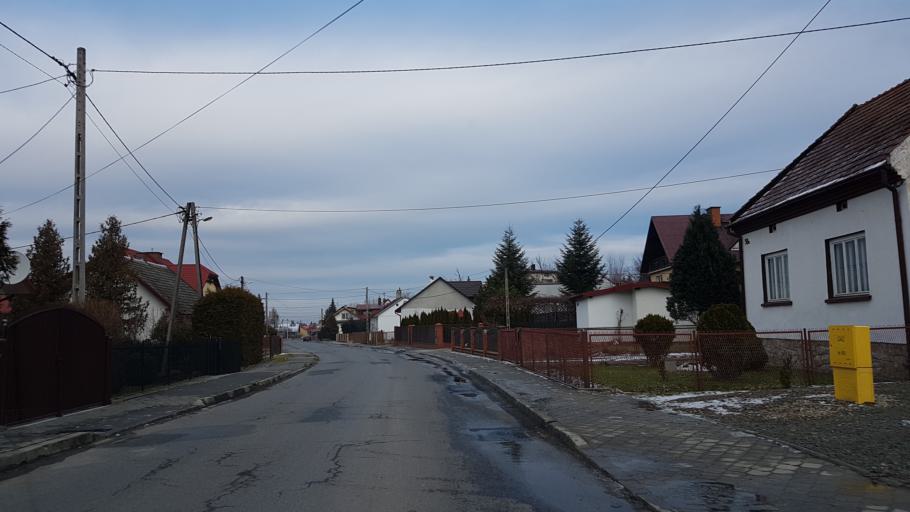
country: PL
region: Lesser Poland Voivodeship
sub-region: Powiat nowosadecki
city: Stary Sacz
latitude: 49.5498
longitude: 20.6293
